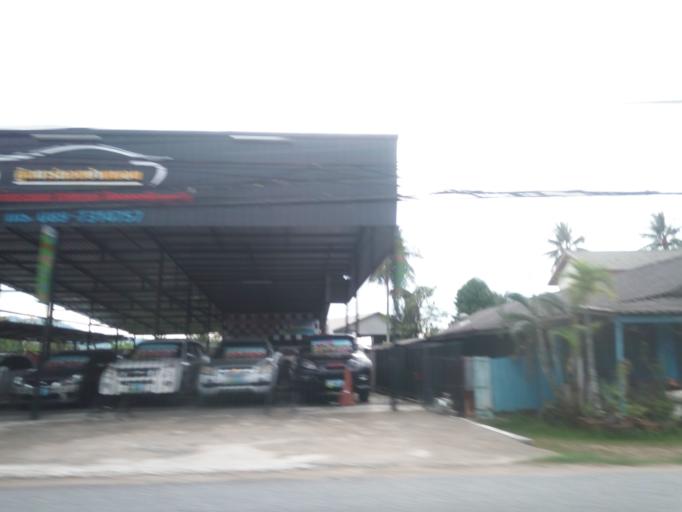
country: TH
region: Phuket
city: Thalang
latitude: 8.0100
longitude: 98.3413
